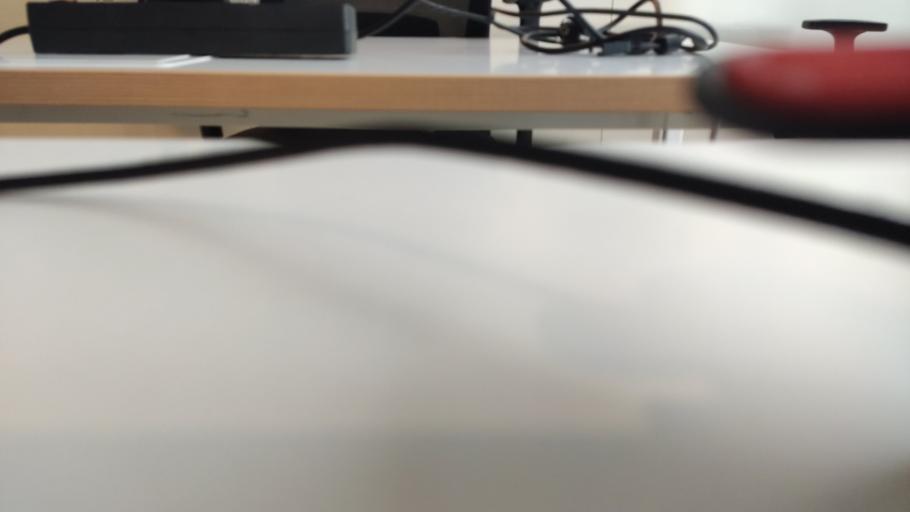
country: RU
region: Moskovskaya
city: Rogachevo
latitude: 56.4111
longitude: 37.0551
